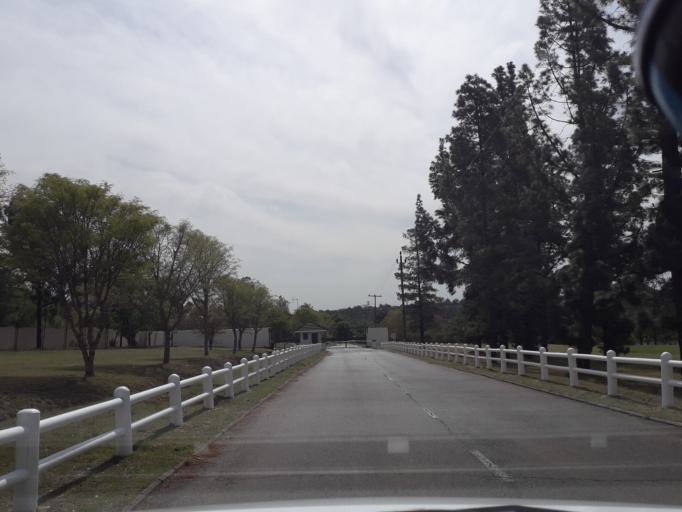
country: ZA
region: Gauteng
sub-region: City of Johannesburg Metropolitan Municipality
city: Diepsloot
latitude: -25.9786
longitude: 28.0570
